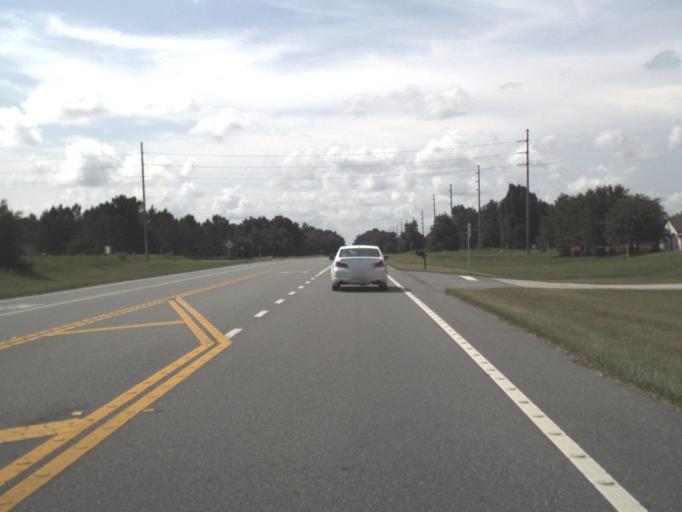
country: US
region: Florida
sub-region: Citrus County
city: Citrus Springs
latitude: 28.9772
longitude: -82.4269
